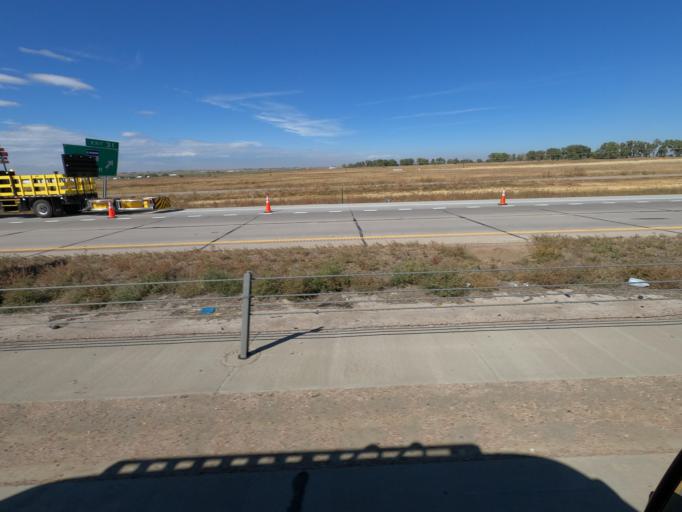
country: US
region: Colorado
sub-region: Weld County
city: Hudson
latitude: 40.0791
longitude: -104.6417
